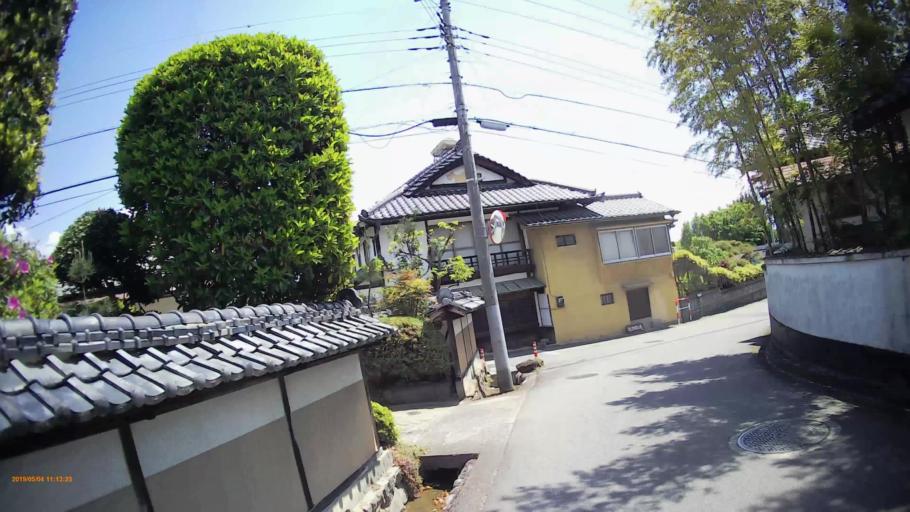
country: JP
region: Yamanashi
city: Nirasaki
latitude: 35.6963
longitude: 138.4714
